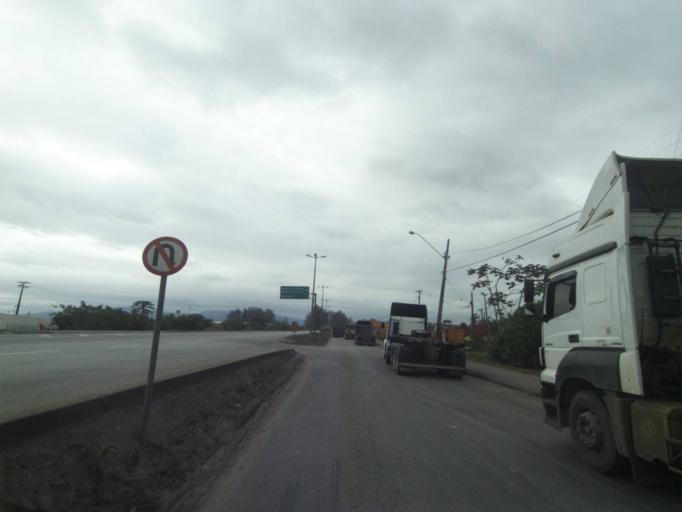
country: BR
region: Parana
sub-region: Paranagua
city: Paranagua
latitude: -25.5446
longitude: -48.5596
